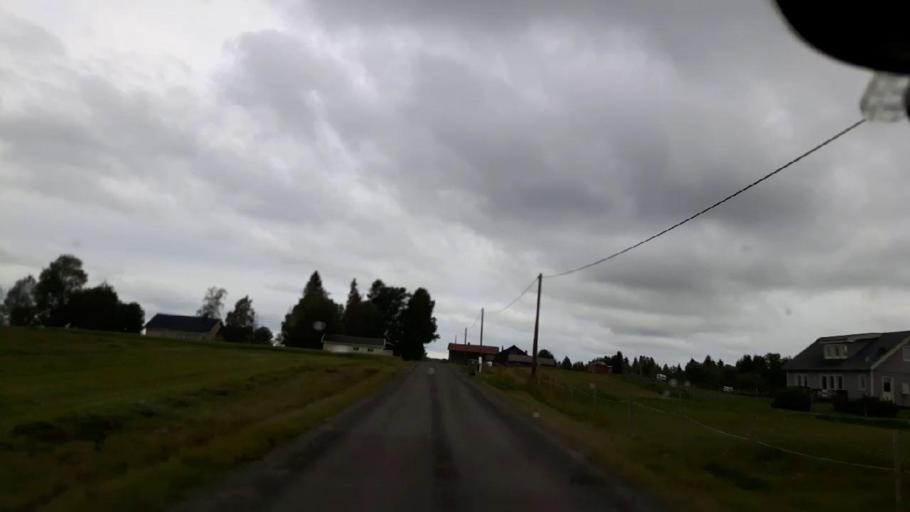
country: SE
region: Jaemtland
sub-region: OEstersunds Kommun
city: Ostersund
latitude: 63.0532
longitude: 14.5651
